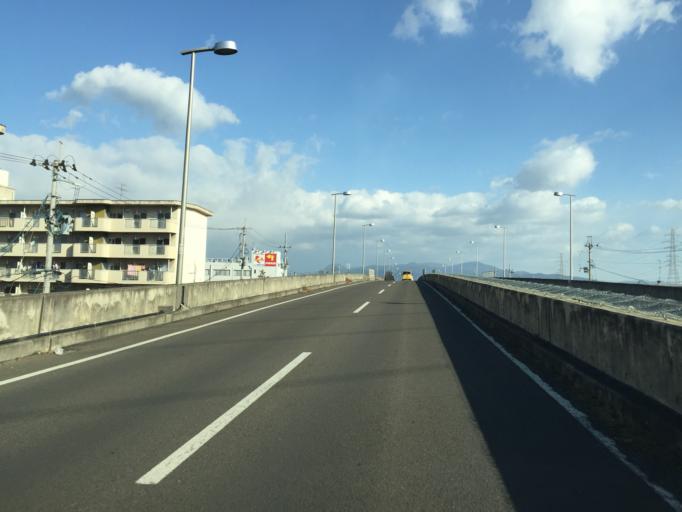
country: JP
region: Fukushima
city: Fukushima-shi
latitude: 37.7634
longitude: 140.4356
